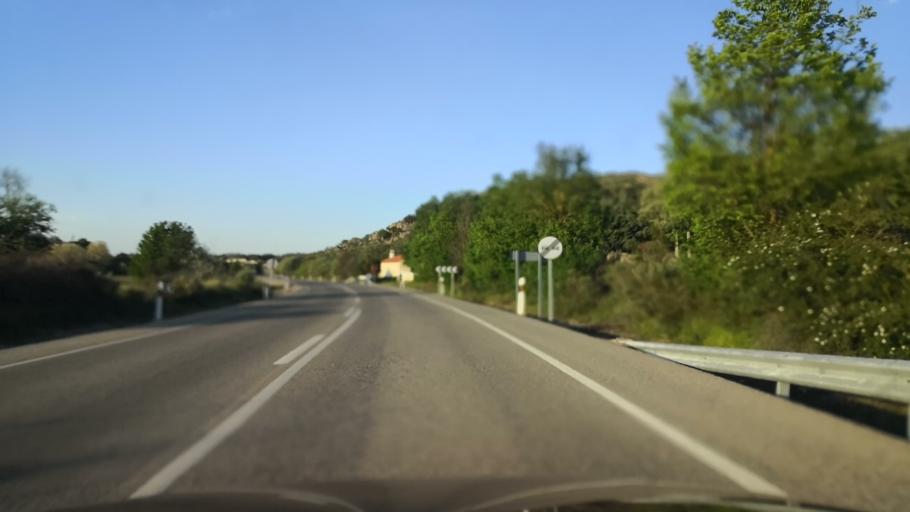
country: ES
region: Extremadura
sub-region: Provincia de Caceres
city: Valencia de Alcantara
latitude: 39.3775
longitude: -7.2532
